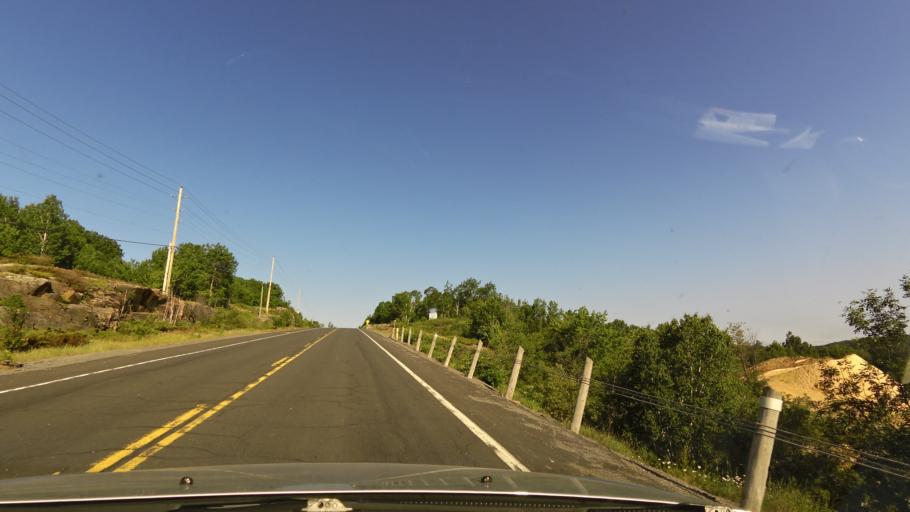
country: CA
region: Ontario
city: Greater Sudbury
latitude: 46.1054
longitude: -80.6414
